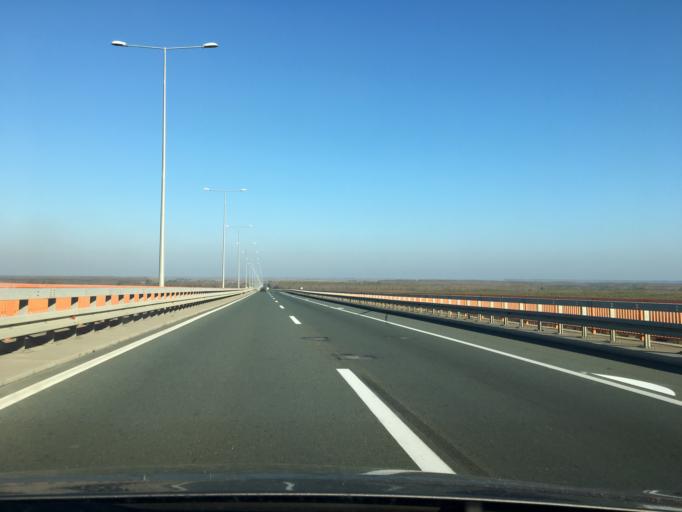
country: RS
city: Beska
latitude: 45.1673
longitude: 20.0803
